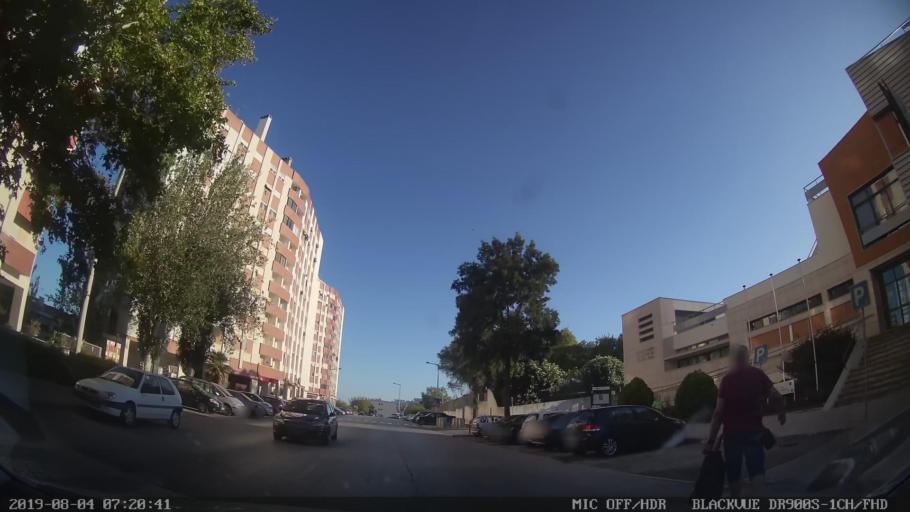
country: PT
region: Lisbon
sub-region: Vila Franca de Xira
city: Povoa de Santa Iria
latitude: 38.8620
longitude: -9.0679
